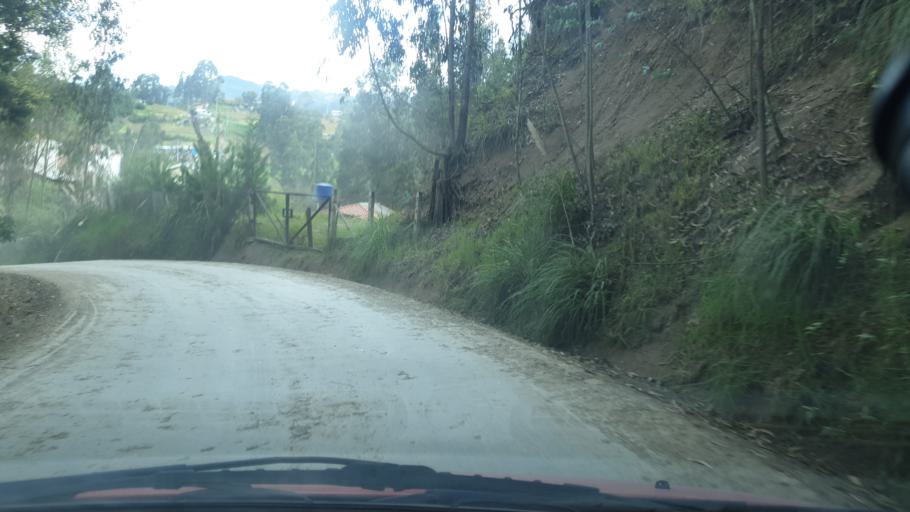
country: EC
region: Azuay
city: Cuenca
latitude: -2.9191
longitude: -78.9788
